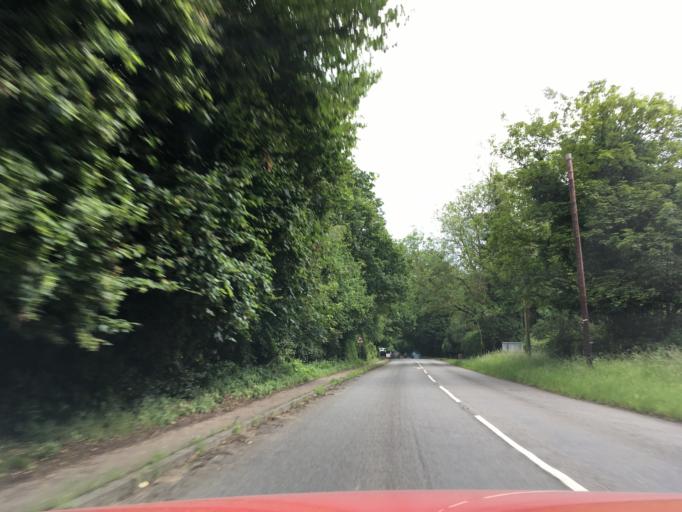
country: GB
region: England
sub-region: Milton Keynes
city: Woburn Sands
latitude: 52.0087
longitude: -0.6449
